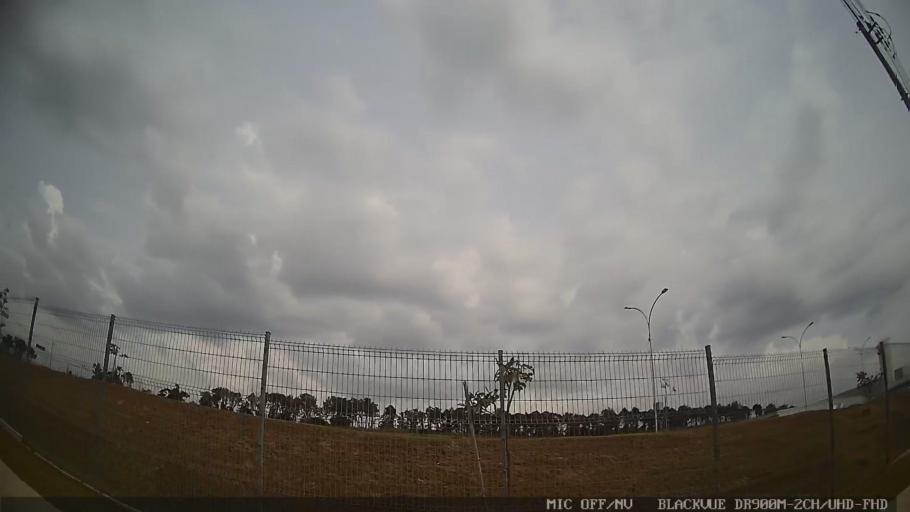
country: BR
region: Sao Paulo
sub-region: Indaiatuba
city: Indaiatuba
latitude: -23.1129
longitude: -47.2776
